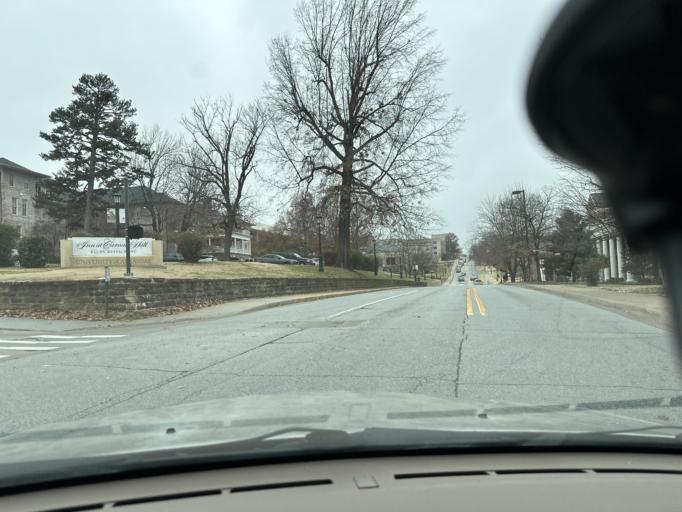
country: US
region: Arkansas
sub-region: Washington County
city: Fayetteville
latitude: 36.0702
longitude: -94.1684
